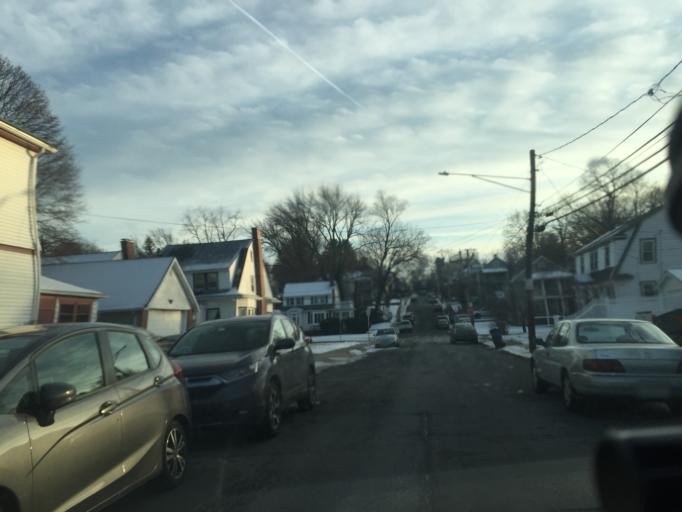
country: US
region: Massachusetts
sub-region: Middlesex County
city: Watertown
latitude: 42.3533
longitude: -71.1581
